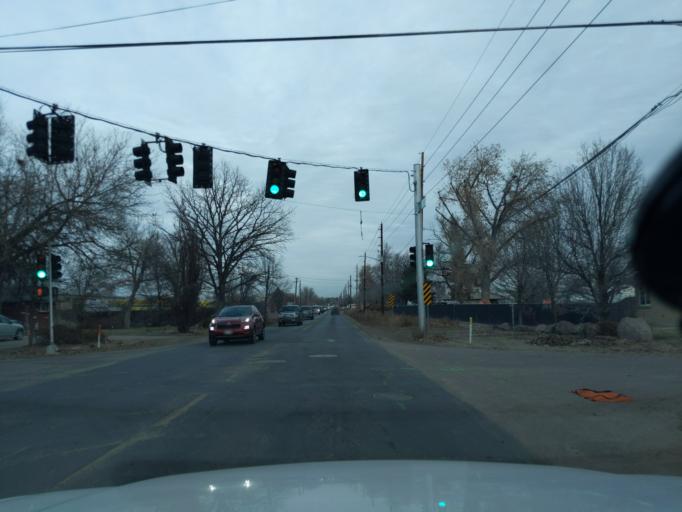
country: US
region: Colorado
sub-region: Adams County
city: Welby
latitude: 39.8307
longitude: -104.9591
